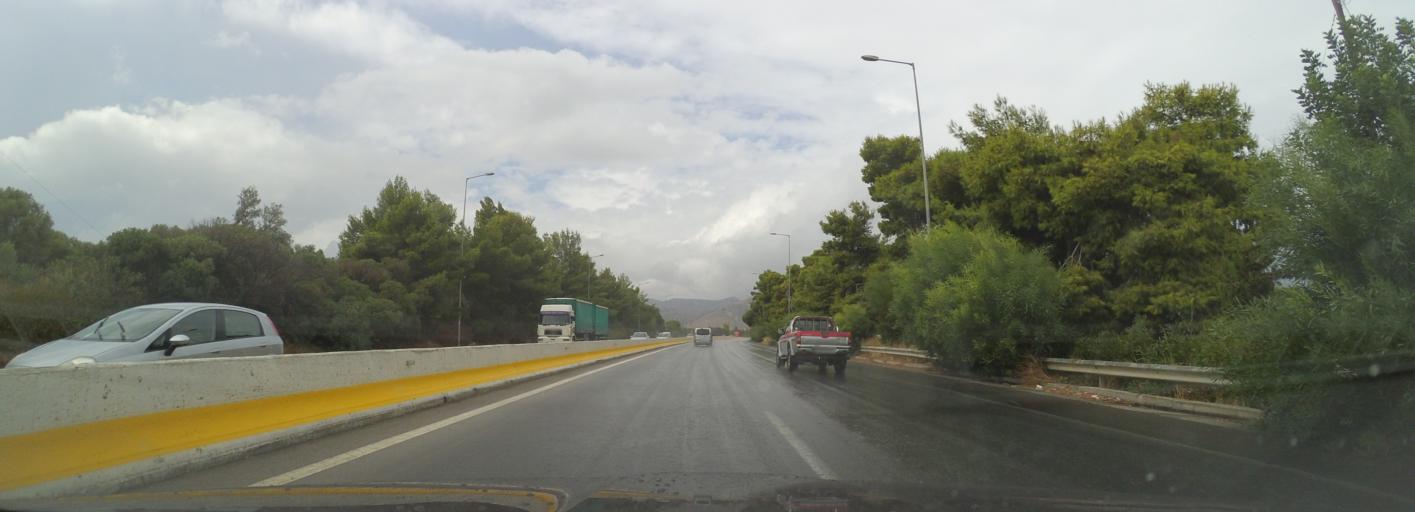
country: GR
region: Crete
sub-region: Nomos Irakleiou
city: Gazi
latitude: 35.3173
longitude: 25.0753
